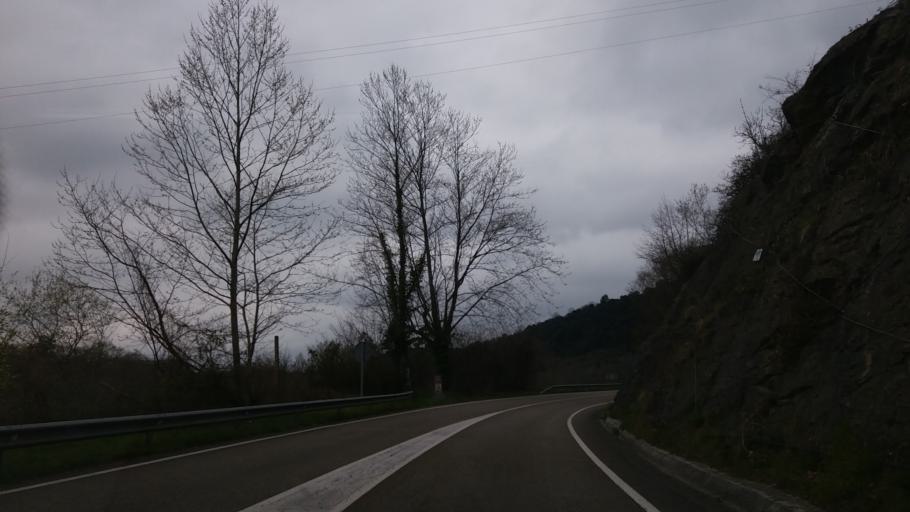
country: ES
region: Cantabria
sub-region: Provincia de Cantabria
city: San Vicente de la Barquera
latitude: 43.3109
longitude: -4.4707
